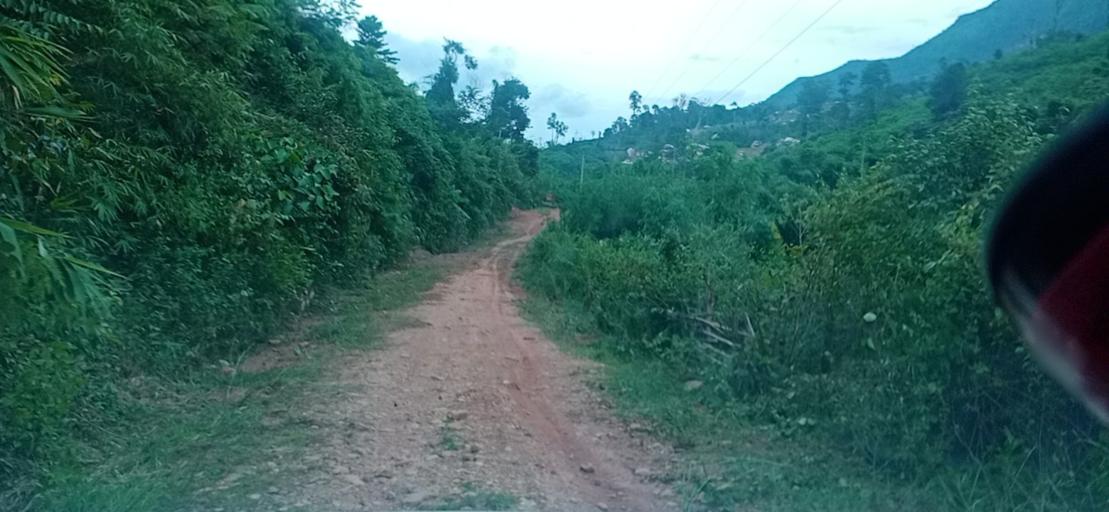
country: TH
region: Changwat Bueng Kan
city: Pak Khat
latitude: 18.5594
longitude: 103.2471
